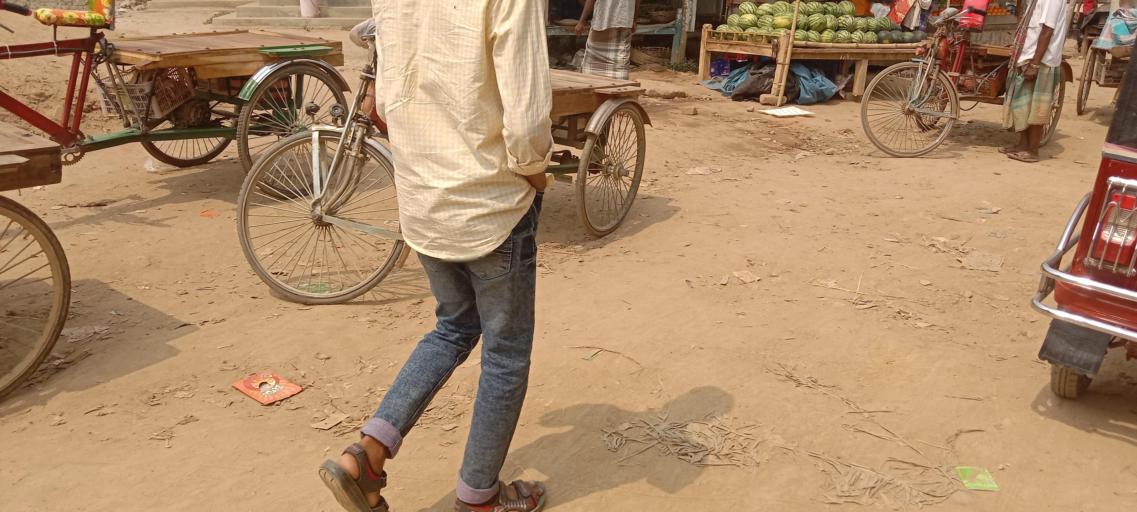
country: BD
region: Dhaka
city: Sakhipur
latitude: 24.3077
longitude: 90.2690
